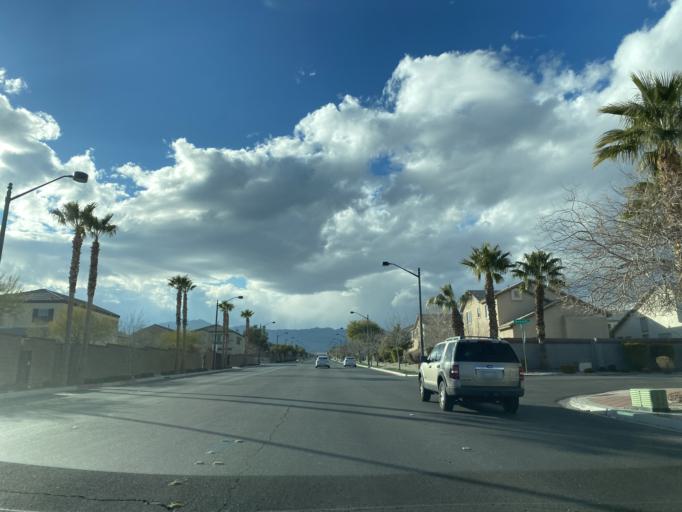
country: US
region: Nevada
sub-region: Clark County
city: Summerlin South
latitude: 36.2846
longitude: -115.2909
